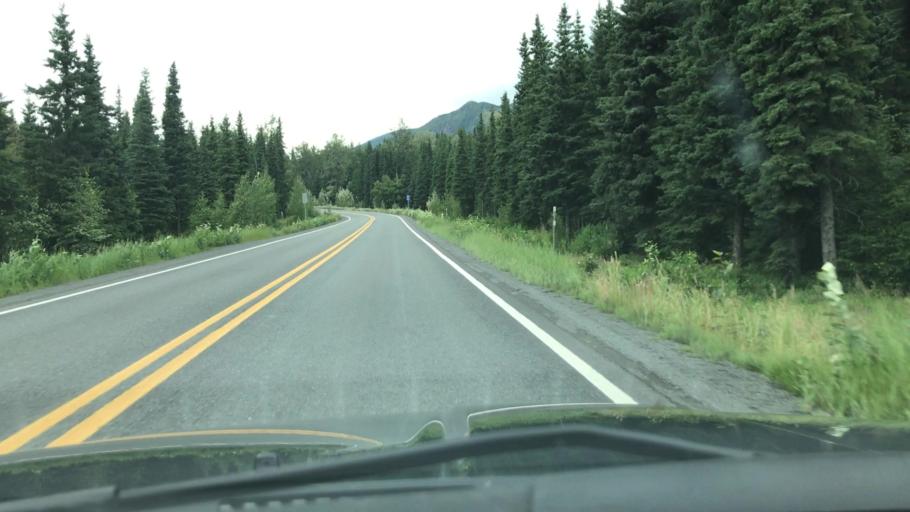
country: US
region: Alaska
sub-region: Kenai Peninsula Borough
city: Seward
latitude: 60.4836
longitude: -149.9436
